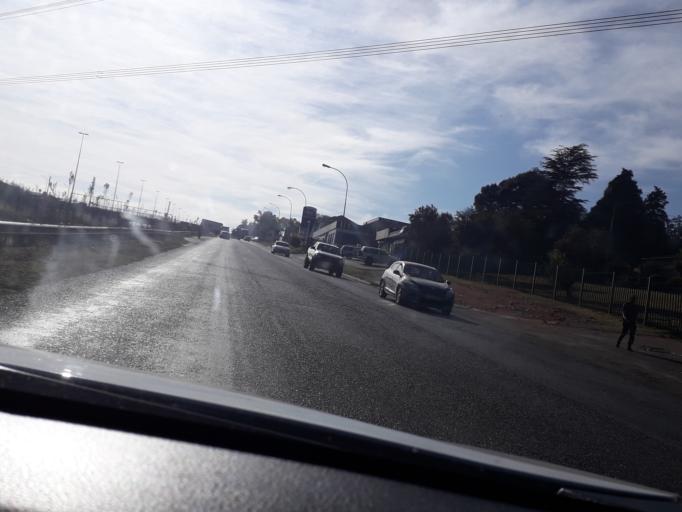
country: ZA
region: Gauteng
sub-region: Ekurhuleni Metropolitan Municipality
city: Germiston
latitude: -26.1649
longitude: 28.1779
